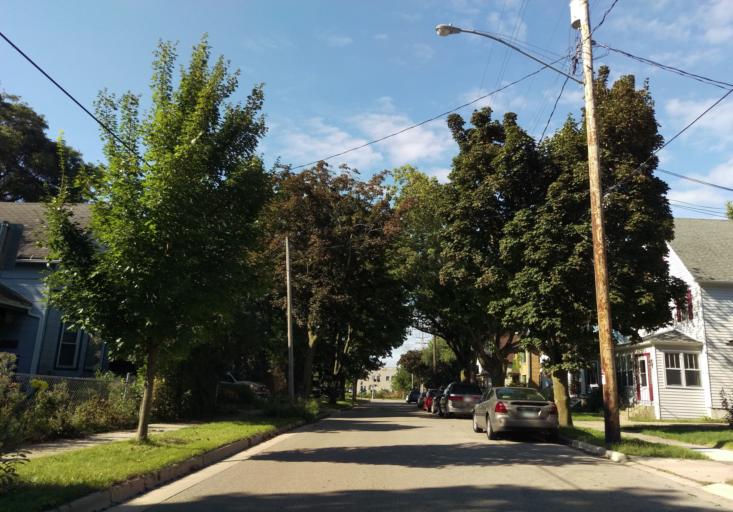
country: US
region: Wisconsin
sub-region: Dane County
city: Maple Bluff
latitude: 43.0923
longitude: -89.3573
